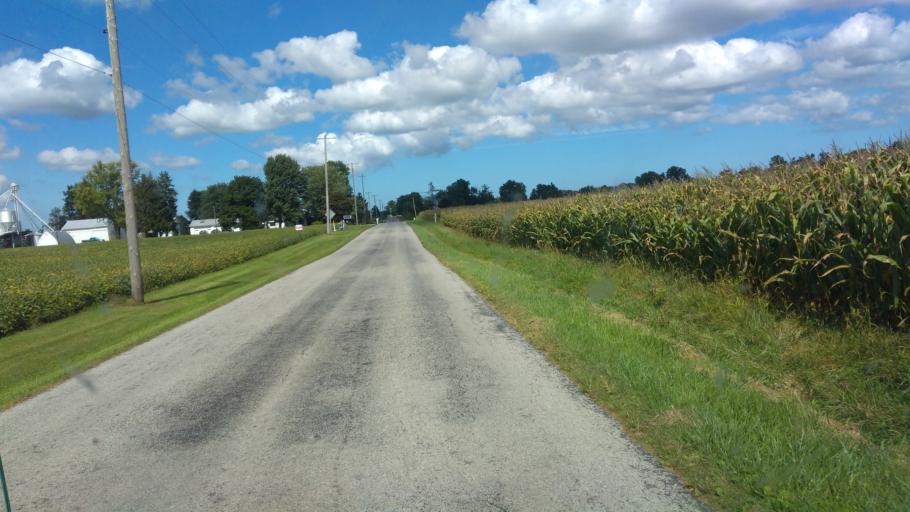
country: US
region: Ohio
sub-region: Huron County
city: Monroeville
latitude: 41.2508
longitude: -82.6659
